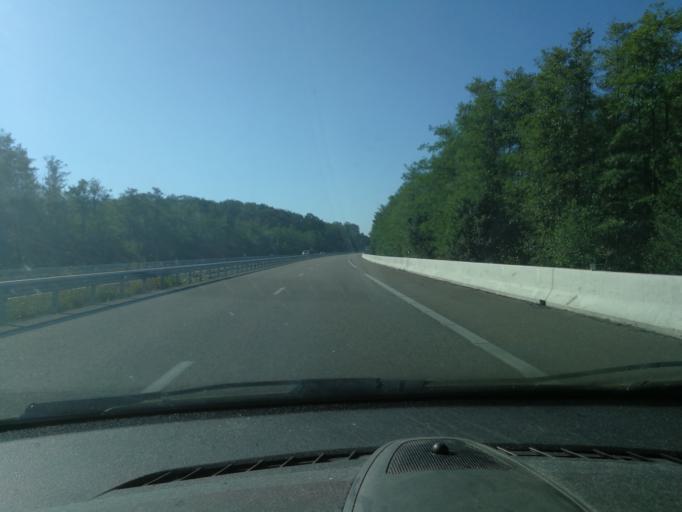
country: FR
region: Lorraine
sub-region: Departement de la Moselle
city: Willerwald
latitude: 49.0322
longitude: 7.0655
